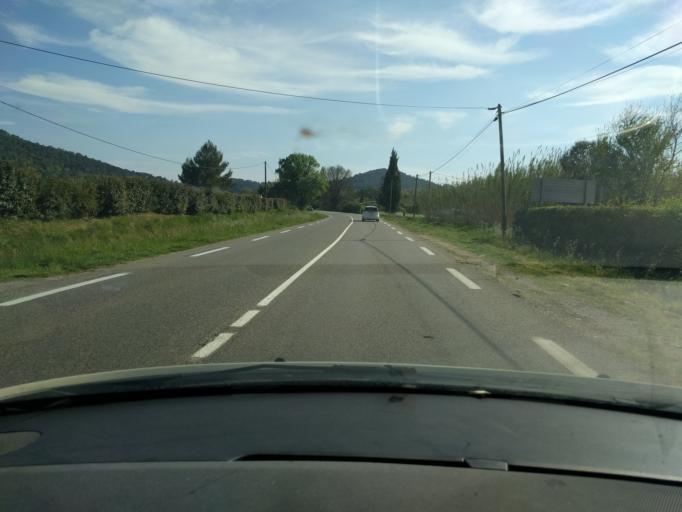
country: FR
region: Provence-Alpes-Cote d'Azur
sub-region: Departement du Var
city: Pierrefeu-du-Var
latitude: 43.1788
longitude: 6.1179
